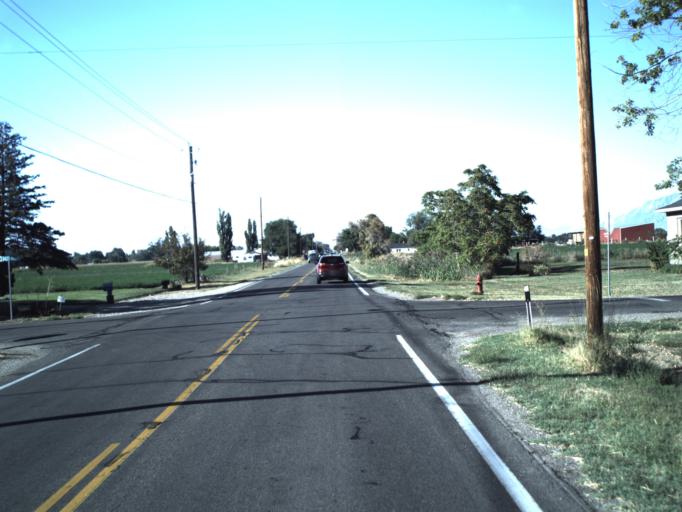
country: US
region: Utah
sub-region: Weber County
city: Hooper
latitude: 41.1487
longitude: -112.1229
